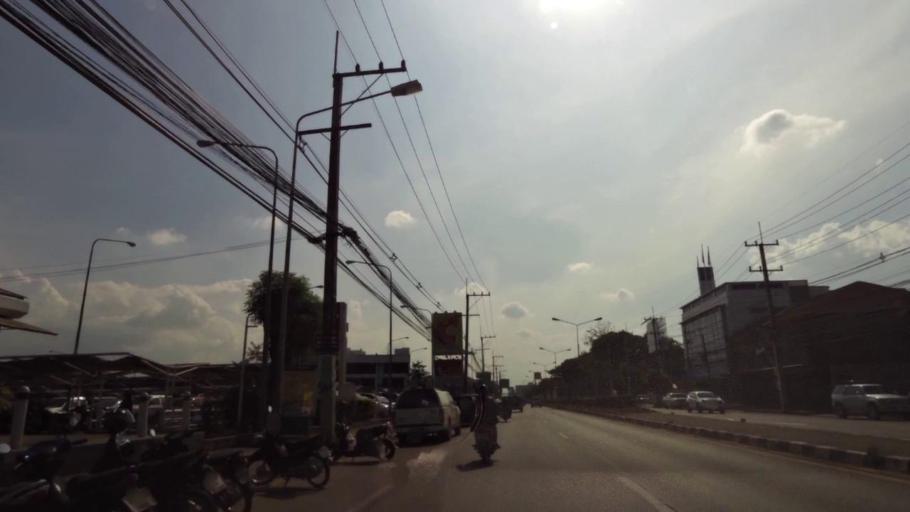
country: TH
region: Phrae
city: Phrae
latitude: 18.1289
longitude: 100.1438
